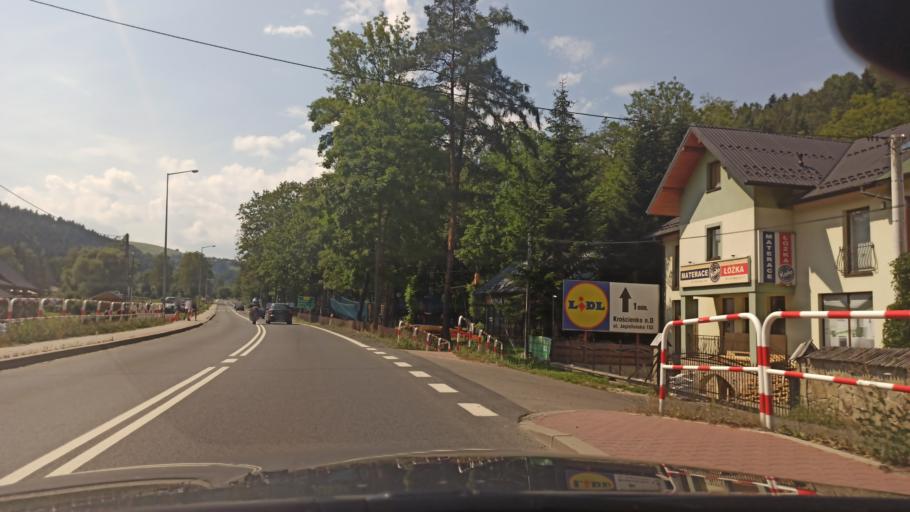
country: PL
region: Lesser Poland Voivodeship
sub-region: Powiat nowotarski
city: Kroscienko nad Dunajcem
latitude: 49.4407
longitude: 20.4168
